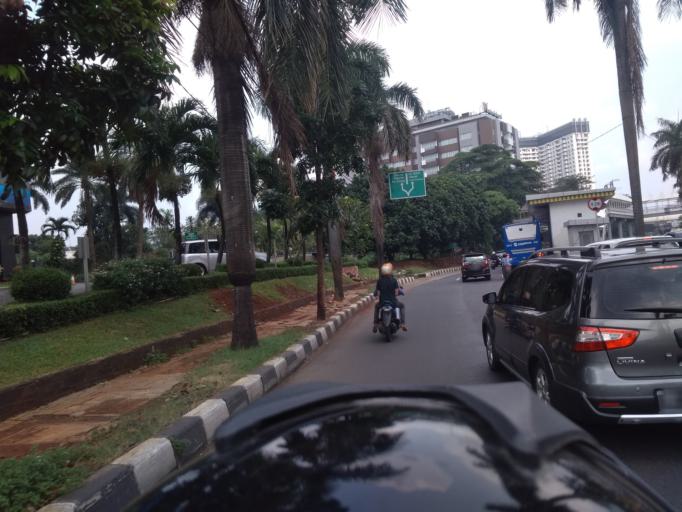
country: ID
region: Banten
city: South Tangerang
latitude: -6.2874
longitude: 106.7794
